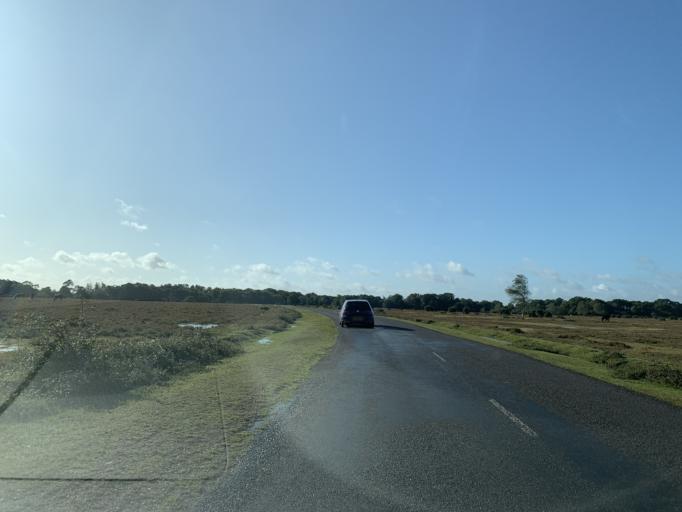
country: GB
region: England
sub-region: Wiltshire
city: Whiteparish
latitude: 50.9372
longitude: -1.6545
